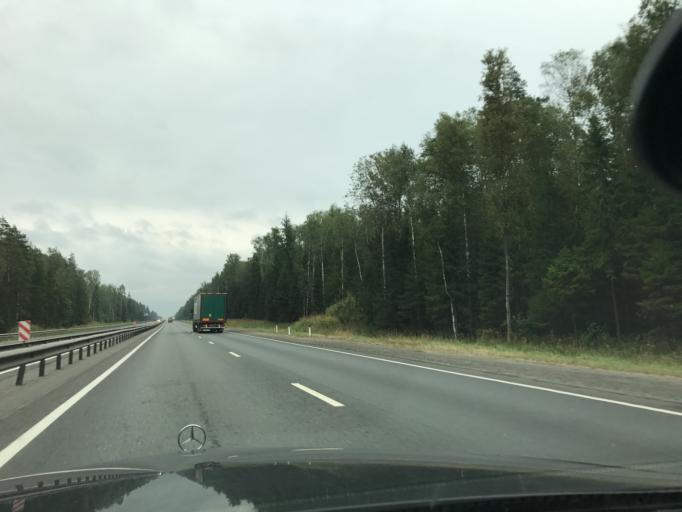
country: RU
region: Vladimir
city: Melekhovo
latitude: 56.2145
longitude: 41.3767
